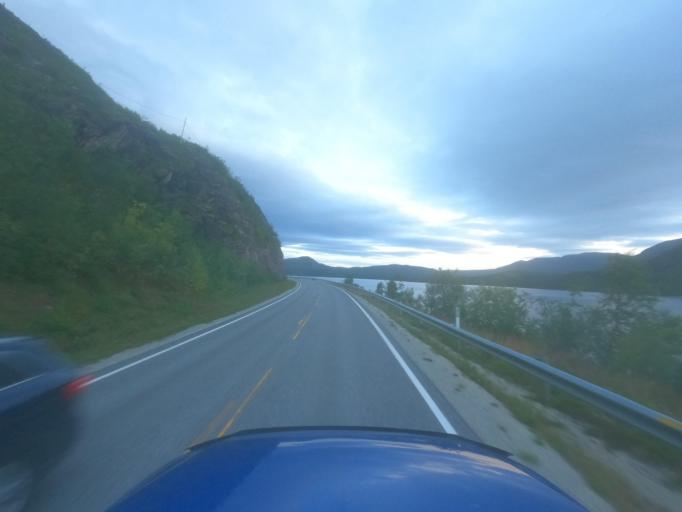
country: NO
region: Finnmark Fylke
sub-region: Porsanger
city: Lakselv
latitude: 69.9182
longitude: 24.9800
